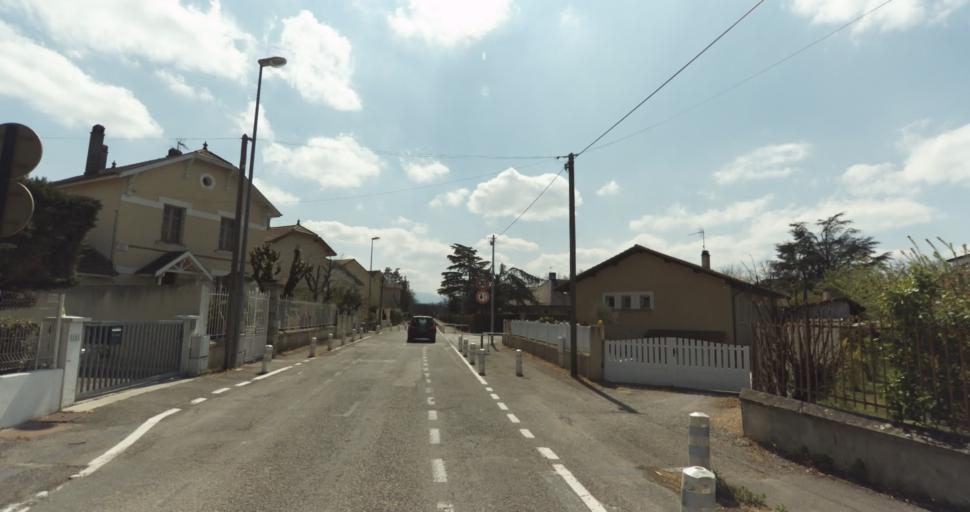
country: FR
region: Rhone-Alpes
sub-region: Departement de l'Isere
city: Saint-Marcellin
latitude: 45.1472
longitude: 5.3204
